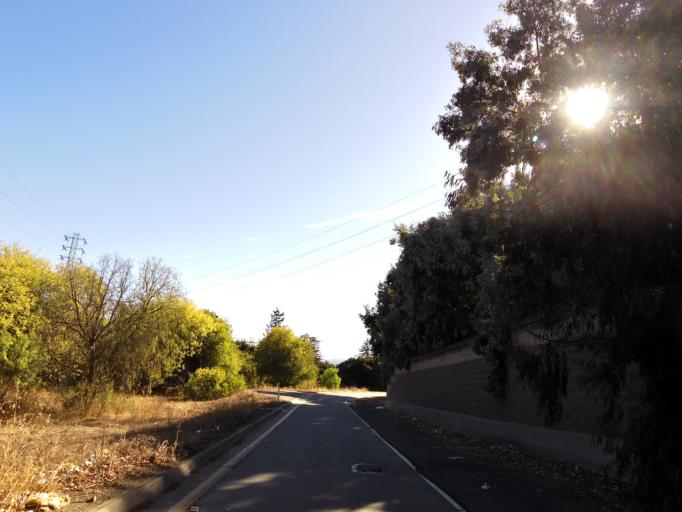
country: US
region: California
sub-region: Santa Clara County
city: Mountain View
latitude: 37.3844
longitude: -122.0698
